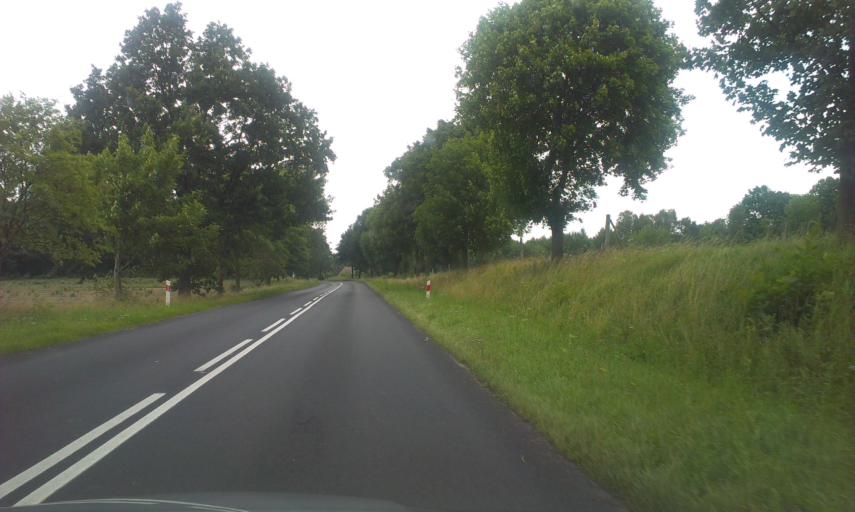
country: PL
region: West Pomeranian Voivodeship
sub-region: Powiat swidwinski
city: Polczyn-Zdroj
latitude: 53.8507
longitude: 16.0745
